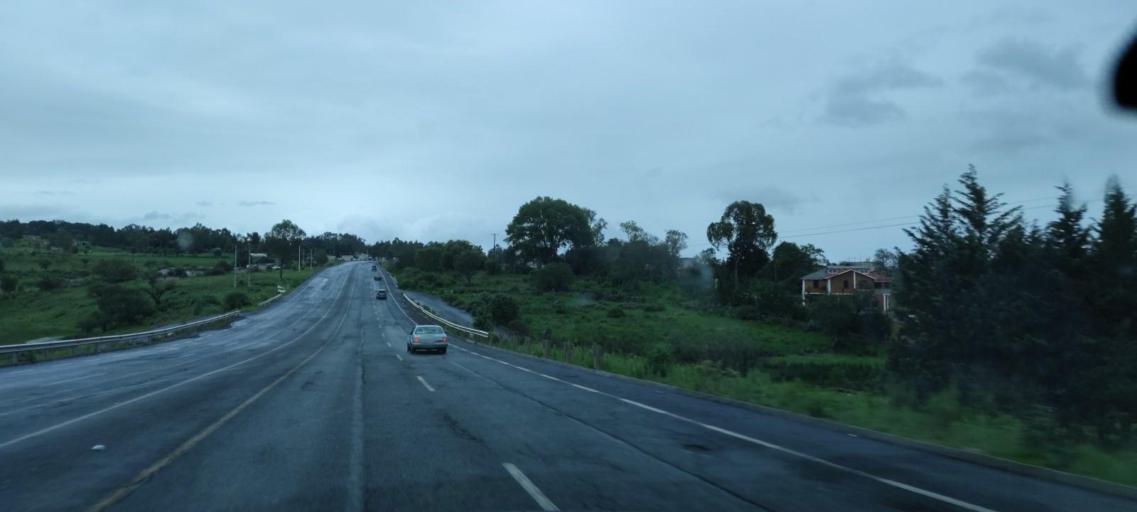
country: MX
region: Mexico
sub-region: Jilotepec
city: Doxhicho
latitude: 19.9052
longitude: -99.6139
